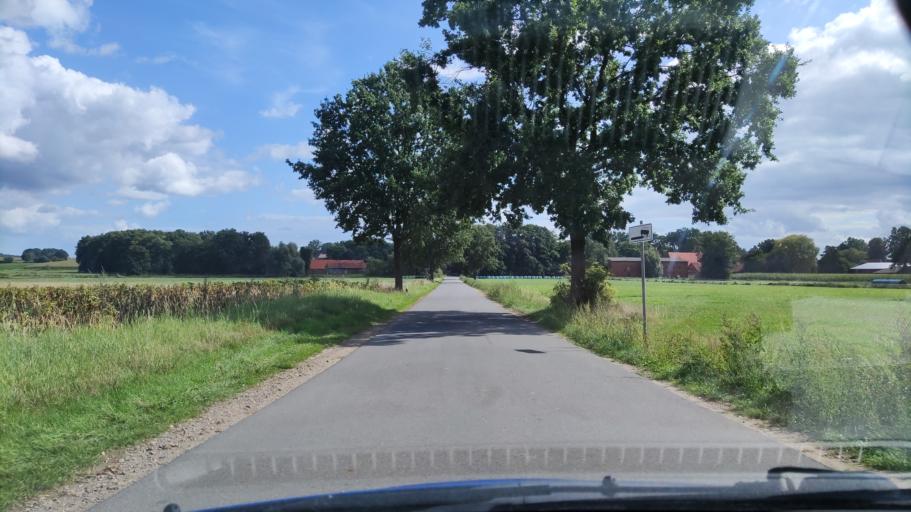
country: DE
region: Lower Saxony
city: Romstedt
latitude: 53.0829
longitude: 10.6376
